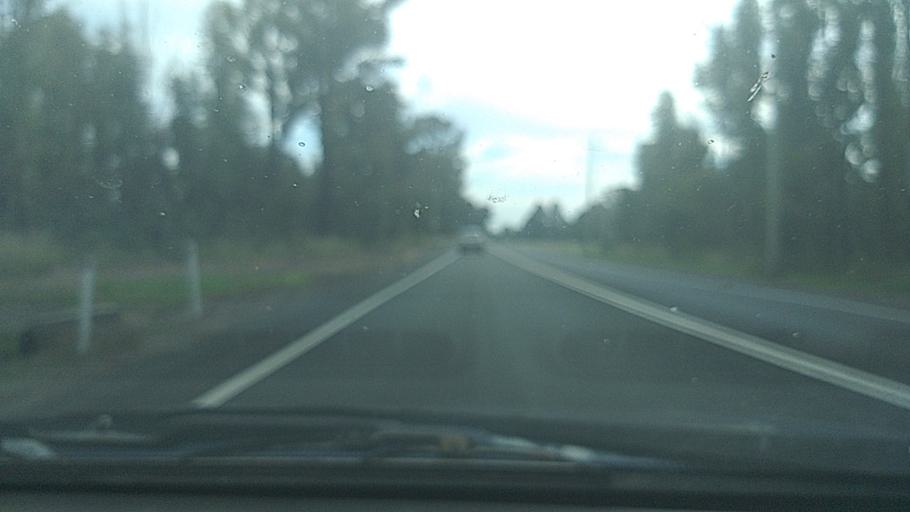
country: AU
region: New South Wales
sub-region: Penrith Municipality
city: Werrington Downs
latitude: -33.7055
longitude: 150.7239
